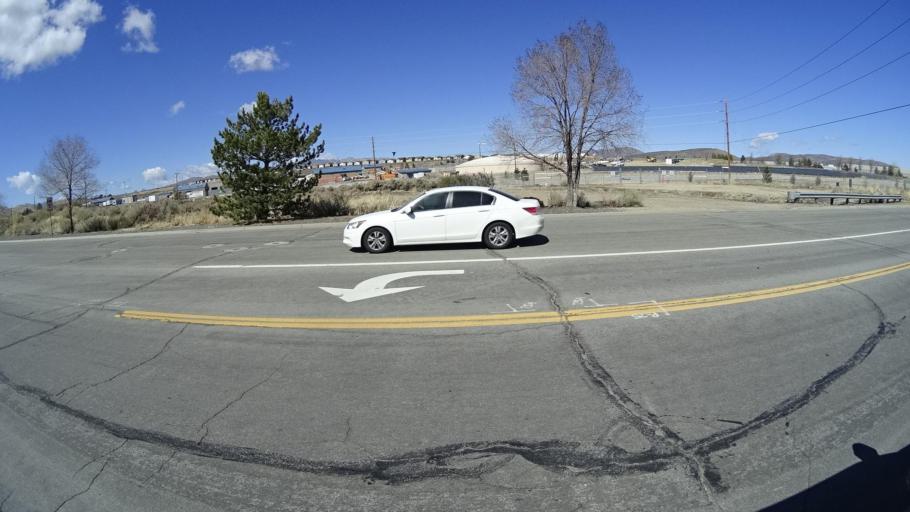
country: US
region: Nevada
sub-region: Washoe County
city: Lemmon Valley
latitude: 39.6426
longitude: -119.8670
